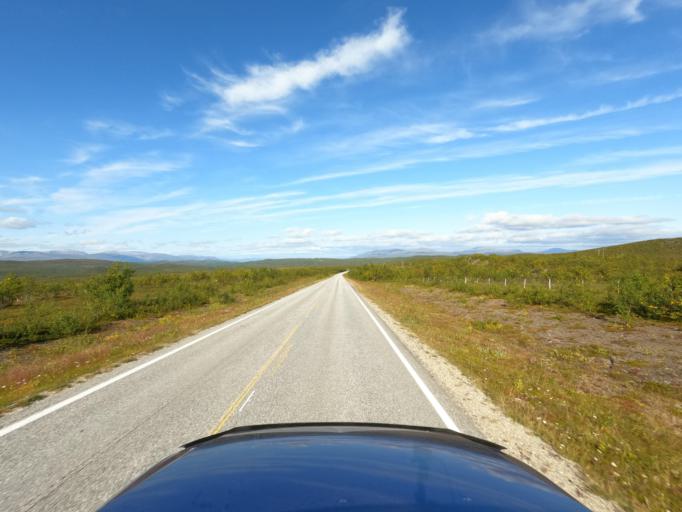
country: NO
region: Finnmark Fylke
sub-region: Karasjok
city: Karasjohka
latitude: 69.7239
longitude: 25.2365
